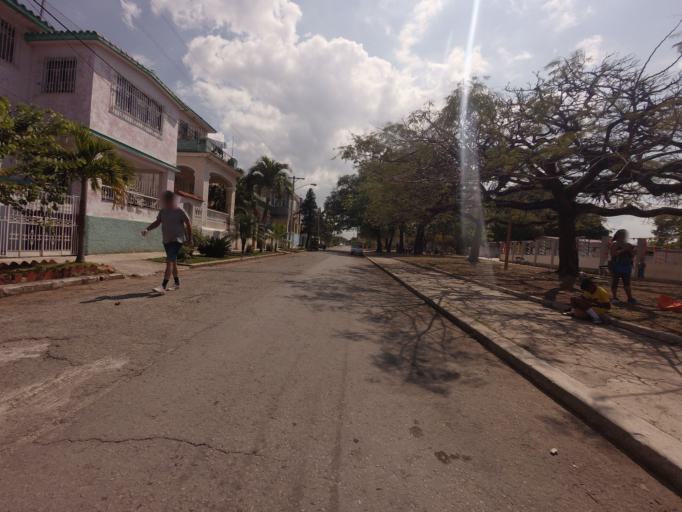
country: CU
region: La Habana
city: Cerro
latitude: 23.1107
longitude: -82.4251
